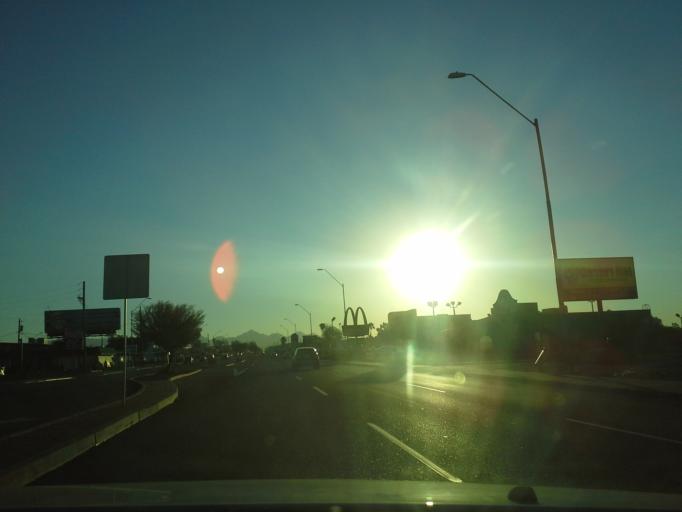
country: US
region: Arizona
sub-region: Maricopa County
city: Paradise Valley
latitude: 33.6405
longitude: -112.0302
